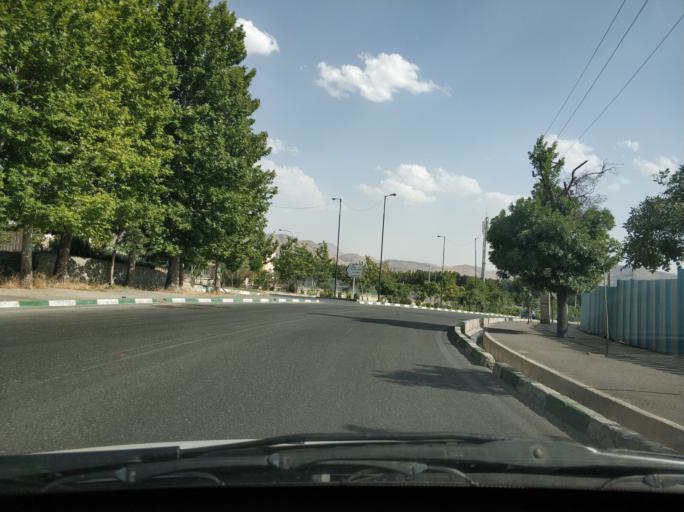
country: IR
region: Tehran
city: Tajrish
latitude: 35.7473
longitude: 51.5770
